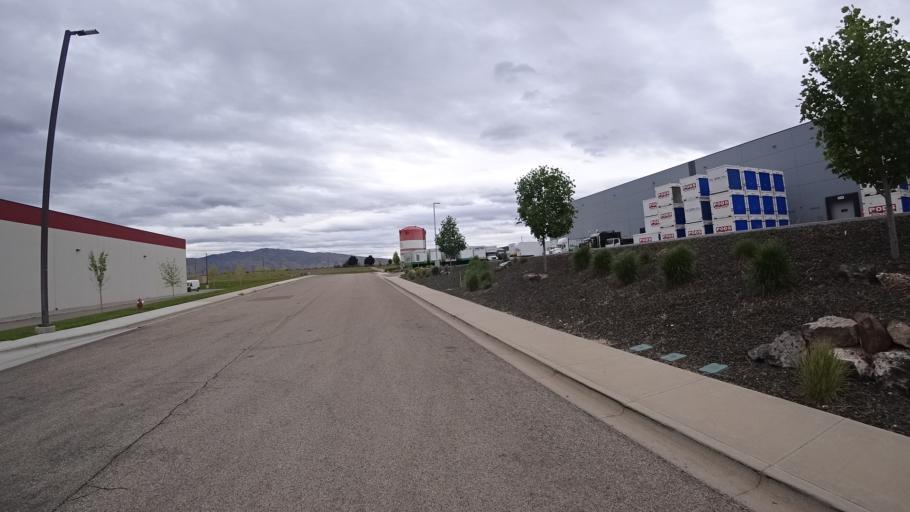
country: US
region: Idaho
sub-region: Ada County
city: Boise
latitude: 43.5402
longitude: -116.1655
